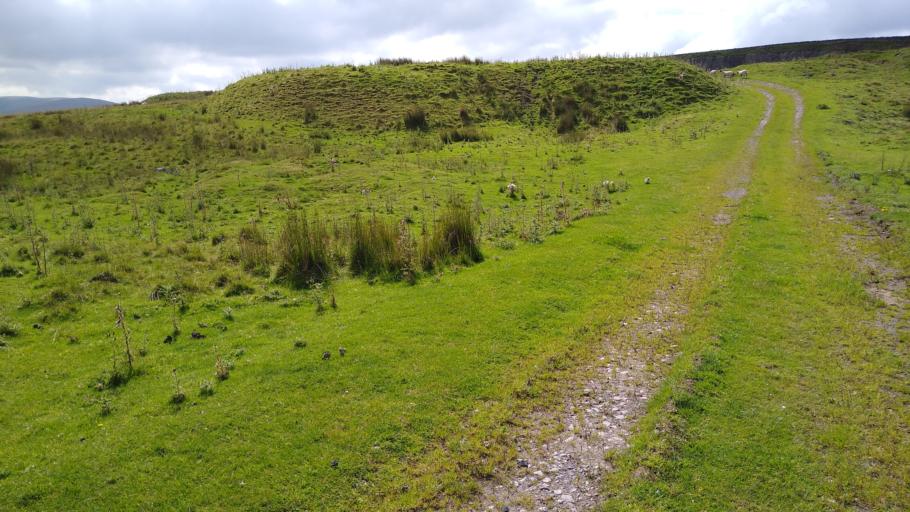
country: GB
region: England
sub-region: Cumbria
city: Wigton
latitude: 54.7520
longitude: -3.1134
